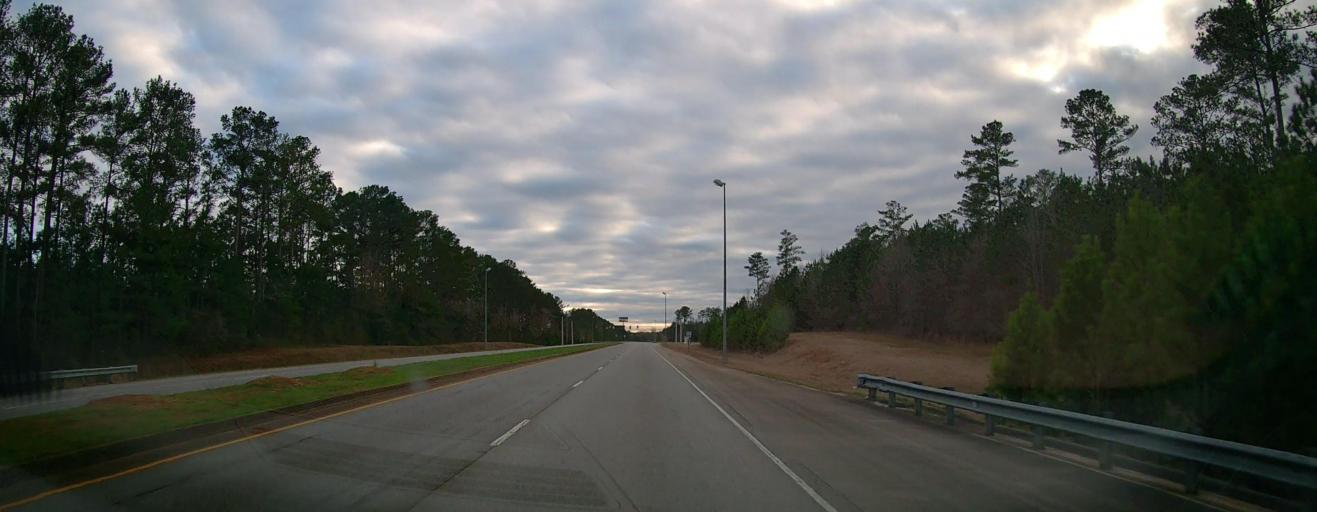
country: US
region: Georgia
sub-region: Troup County
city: West Point
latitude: 32.8929
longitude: -85.1371
